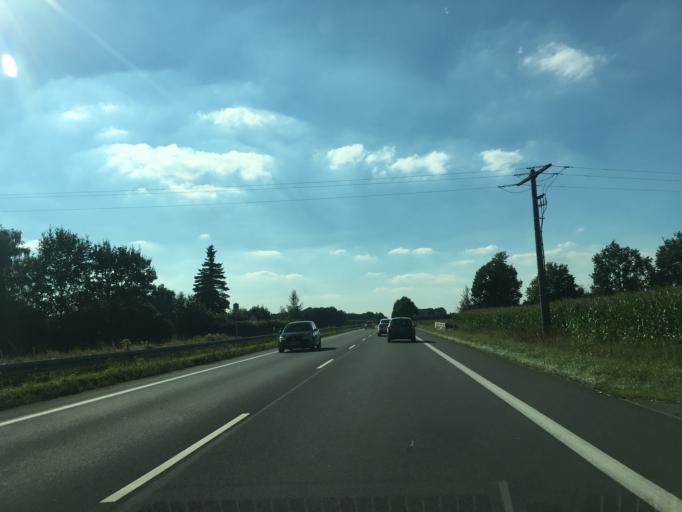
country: DE
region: North Rhine-Westphalia
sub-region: Regierungsbezirk Munster
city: Sassenberg
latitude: 51.9444
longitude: 8.0514
